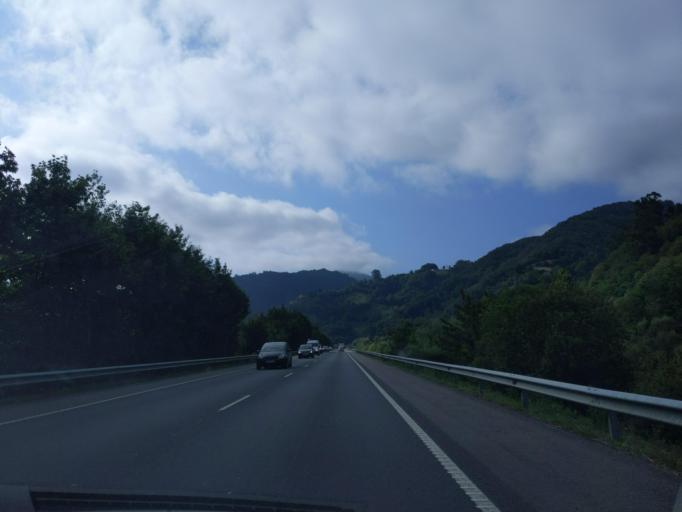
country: ES
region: Asturias
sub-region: Province of Asturias
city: El entrego
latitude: 43.2799
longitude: -5.6181
